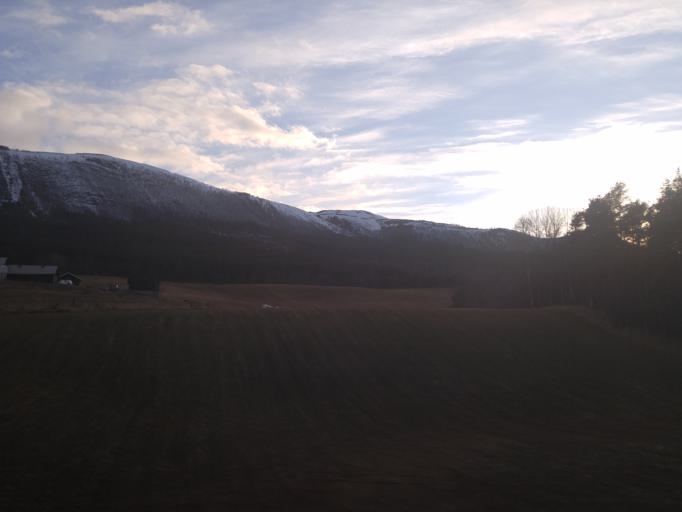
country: NO
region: Oppland
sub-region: Dovre
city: Dovre
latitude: 61.9347
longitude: 9.3036
